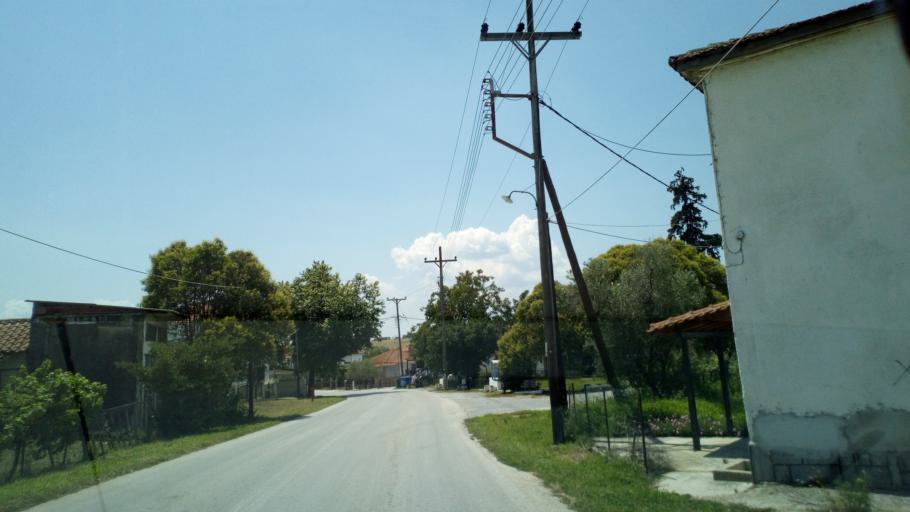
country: GR
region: Central Macedonia
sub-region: Nomos Thessalonikis
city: Askos
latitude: 40.7443
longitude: 23.3880
